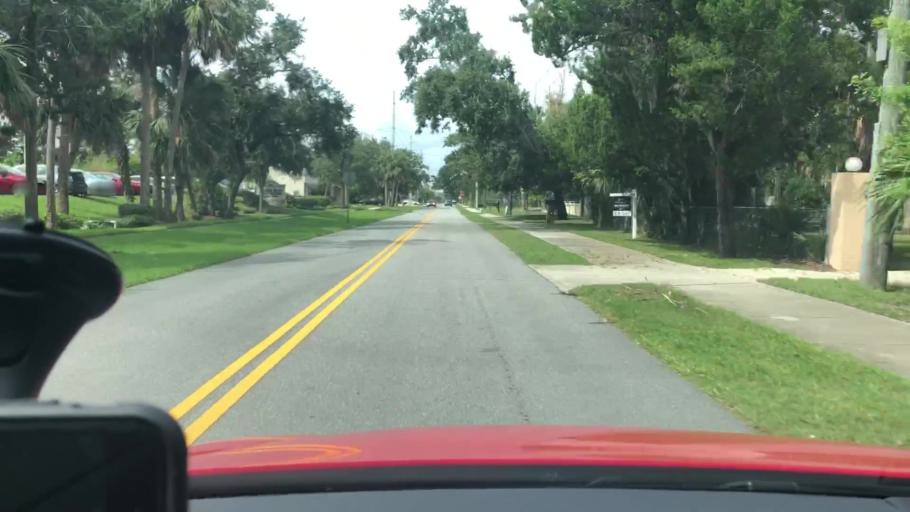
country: US
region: Florida
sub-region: Volusia County
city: South Daytona
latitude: 29.1736
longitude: -81.0010
